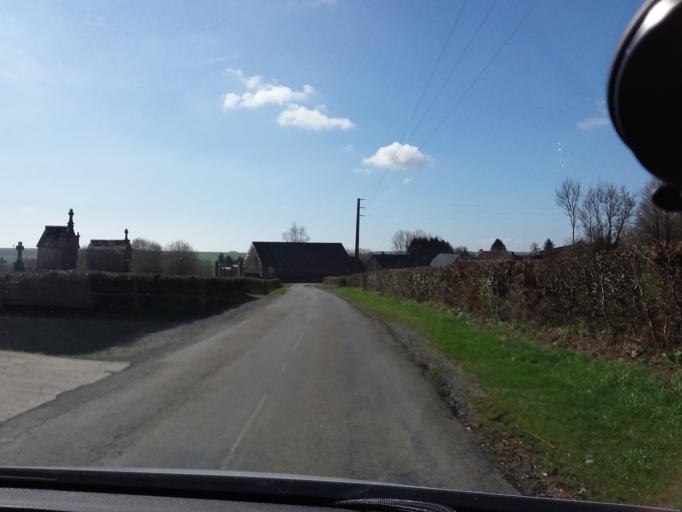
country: FR
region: Picardie
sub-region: Departement de l'Aisne
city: Origny-en-Thierache
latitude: 49.8128
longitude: 4.0248
